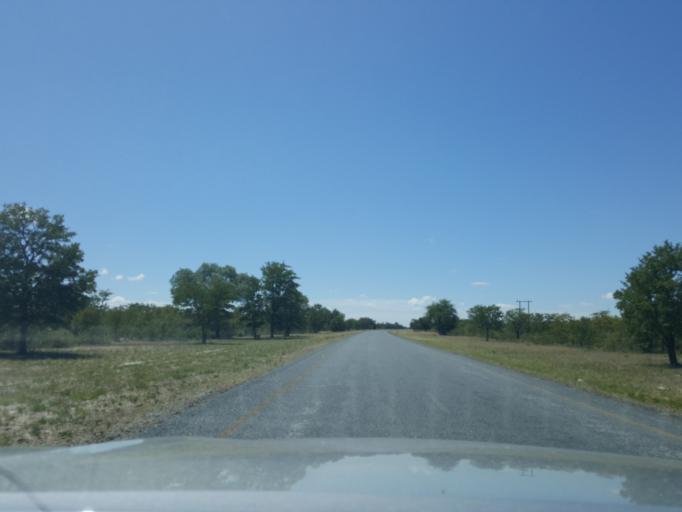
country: BW
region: Central
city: Gweta
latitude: -20.1800
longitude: 25.3200
